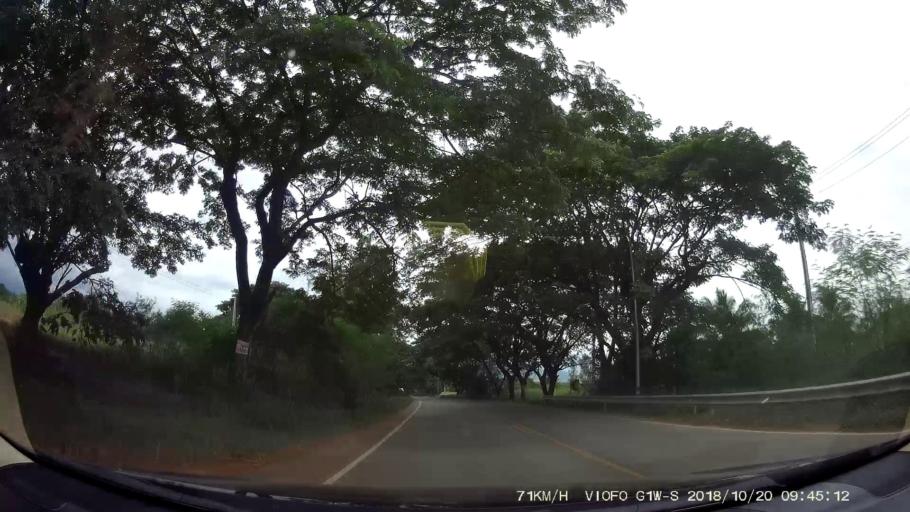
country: TH
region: Chaiyaphum
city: Khon San
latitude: 16.4899
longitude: 101.9391
